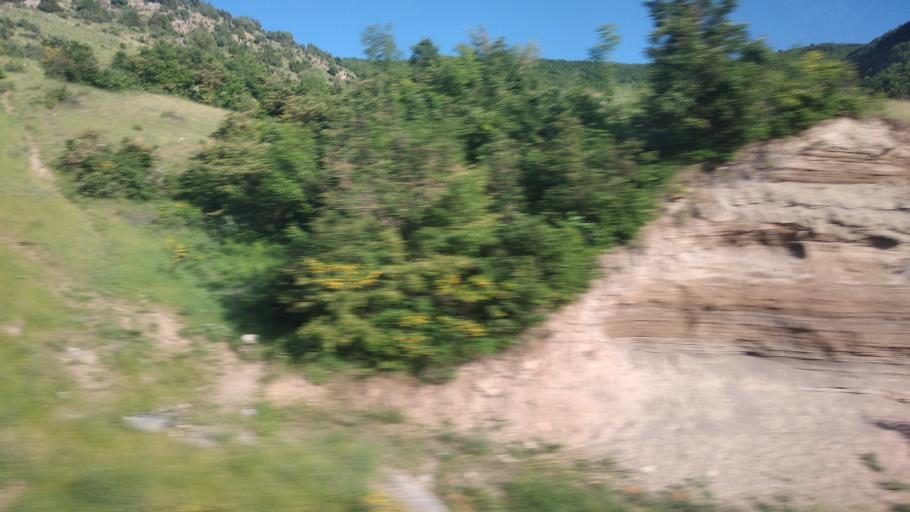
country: TR
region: Bitlis
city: Resadiye
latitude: 38.4754
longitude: 42.5285
